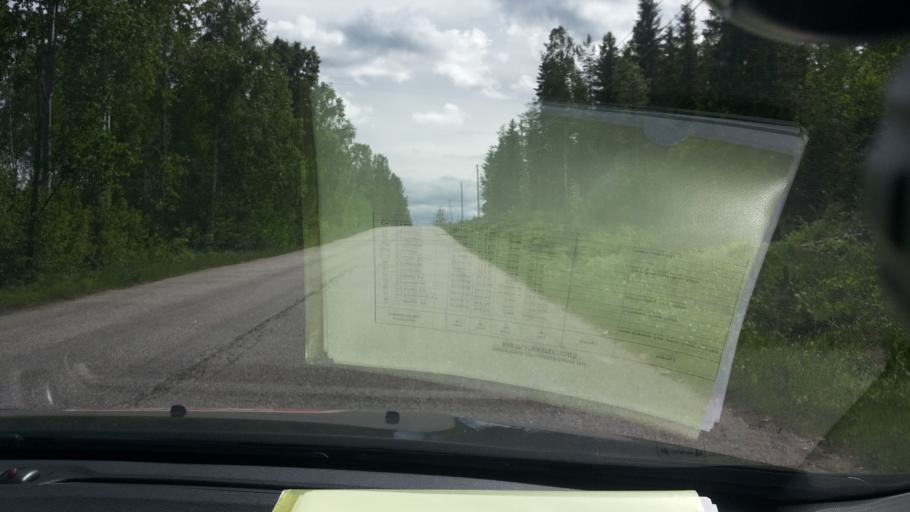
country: SE
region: Vaesternorrland
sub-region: Sundsvalls Kommun
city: Njurundabommen
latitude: 62.1634
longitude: 17.3547
